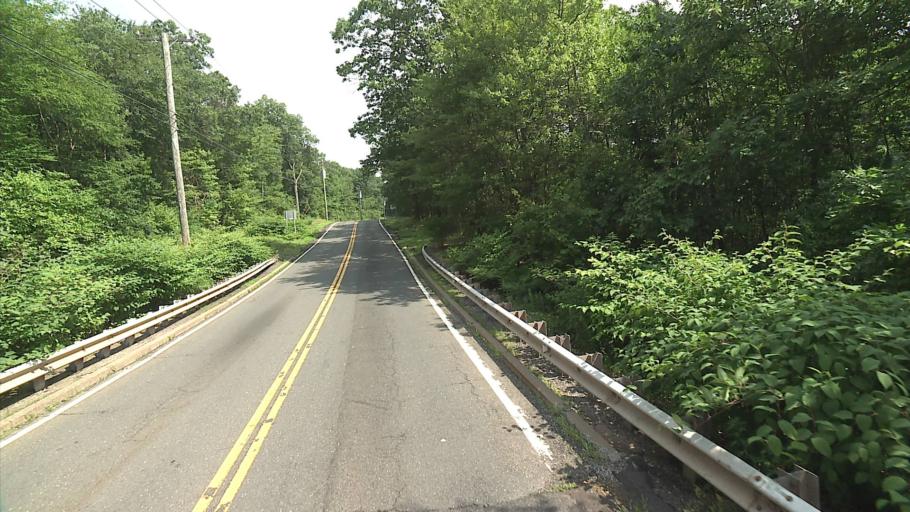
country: US
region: Connecticut
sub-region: New Haven County
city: Wolcott
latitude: 41.5809
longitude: -72.9520
